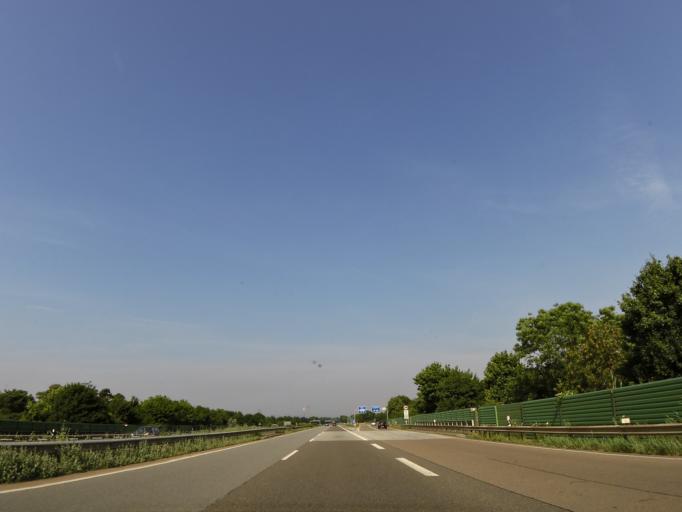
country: DE
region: Rheinland-Pfalz
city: Otterstadt
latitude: 49.3536
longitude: 8.4294
